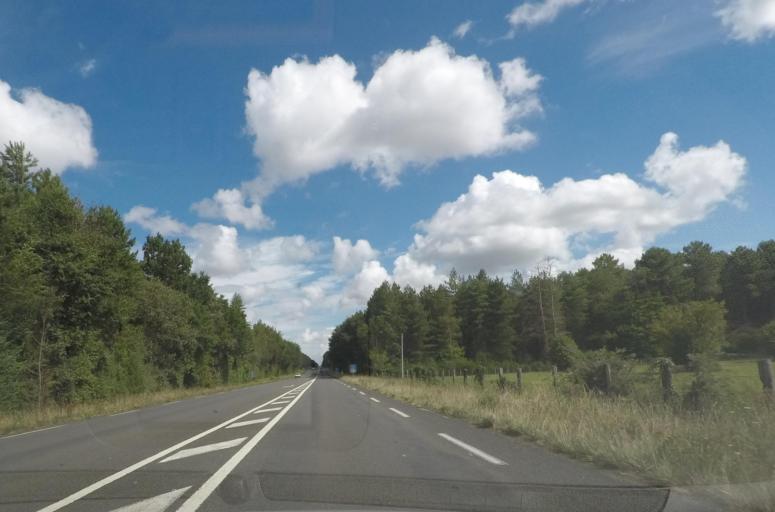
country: FR
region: Pays de la Loire
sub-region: Departement de la Sarthe
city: Cerans-Foulletourte
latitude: 47.7786
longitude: 0.0308
